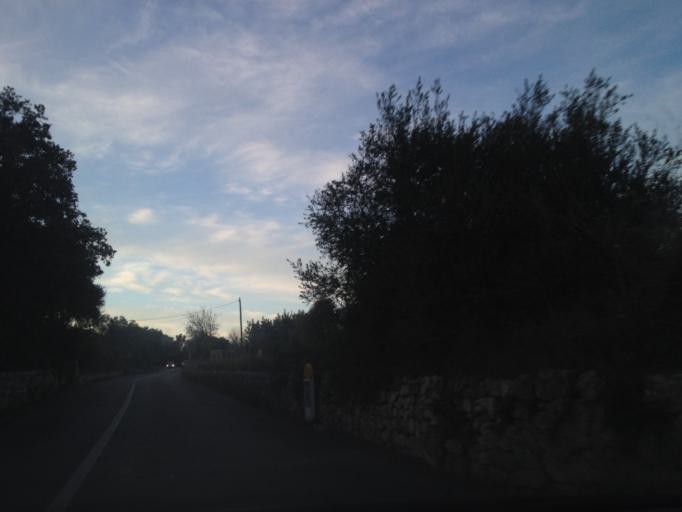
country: ES
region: Balearic Islands
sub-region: Illes Balears
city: Pollenca
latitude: 39.8627
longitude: 3.0460
